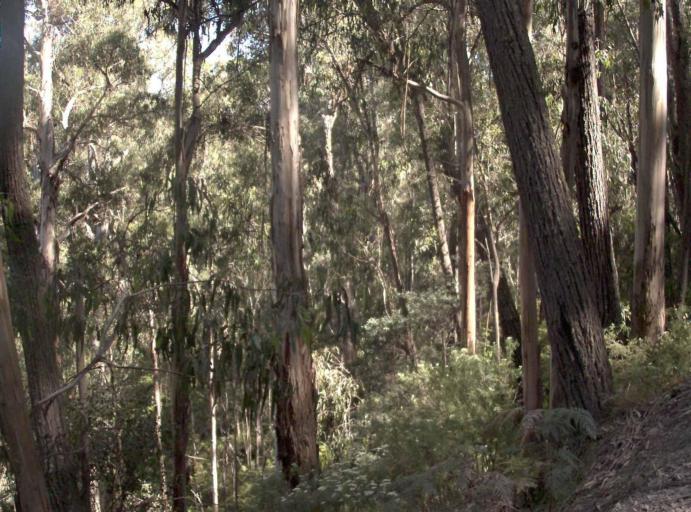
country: AU
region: New South Wales
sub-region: Bombala
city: Bombala
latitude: -37.2574
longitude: 148.7338
